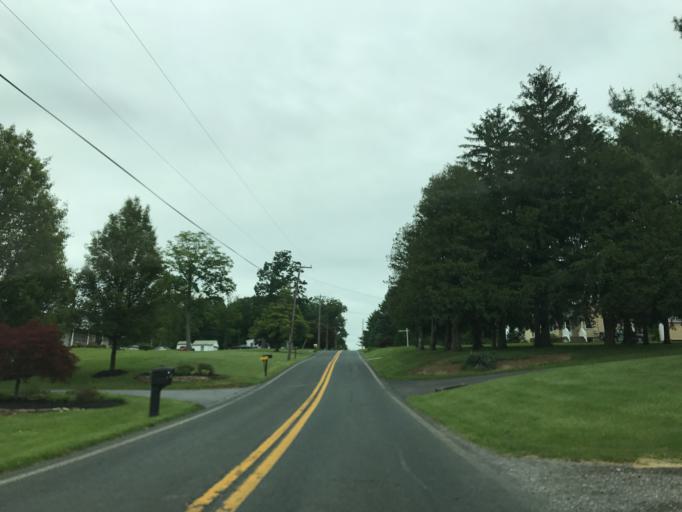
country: US
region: Maryland
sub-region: Carroll County
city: Hampstead
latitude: 39.5978
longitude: -76.8746
